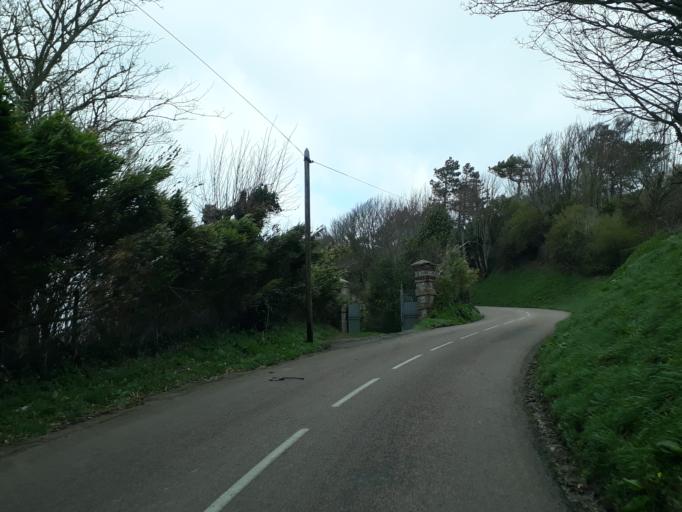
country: FR
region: Haute-Normandie
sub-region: Departement de la Seine-Maritime
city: Yport
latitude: 49.7369
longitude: 0.2930
